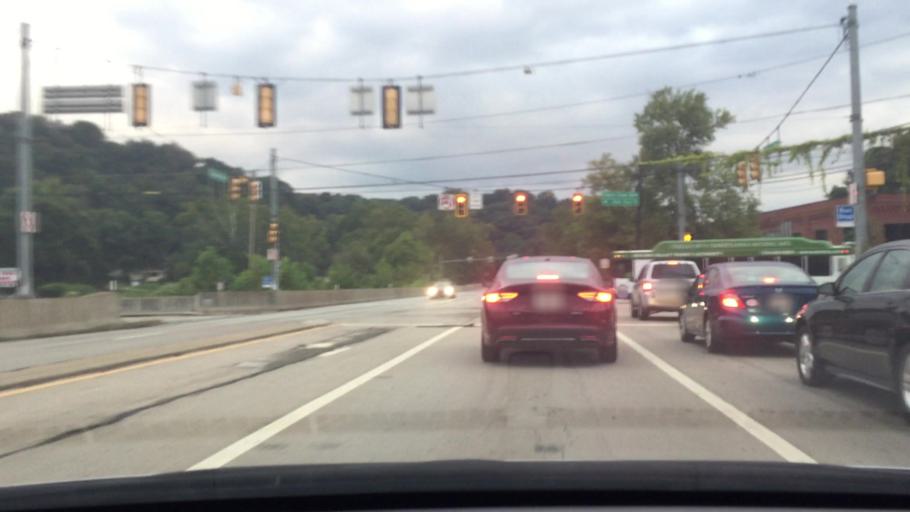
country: US
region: Pennsylvania
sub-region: Allegheny County
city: Jefferson Hills
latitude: 40.2922
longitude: -79.9153
